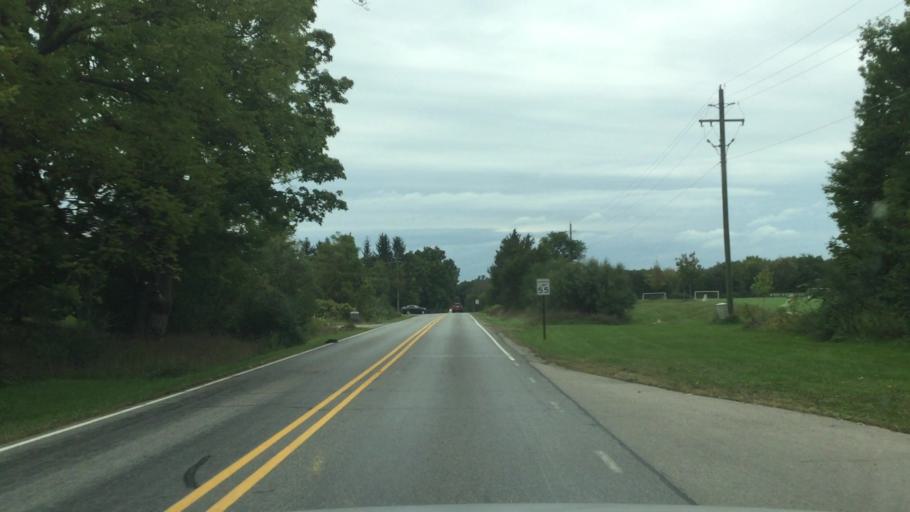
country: US
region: Michigan
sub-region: Livingston County
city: Whitmore Lake
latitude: 42.4662
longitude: -83.7664
